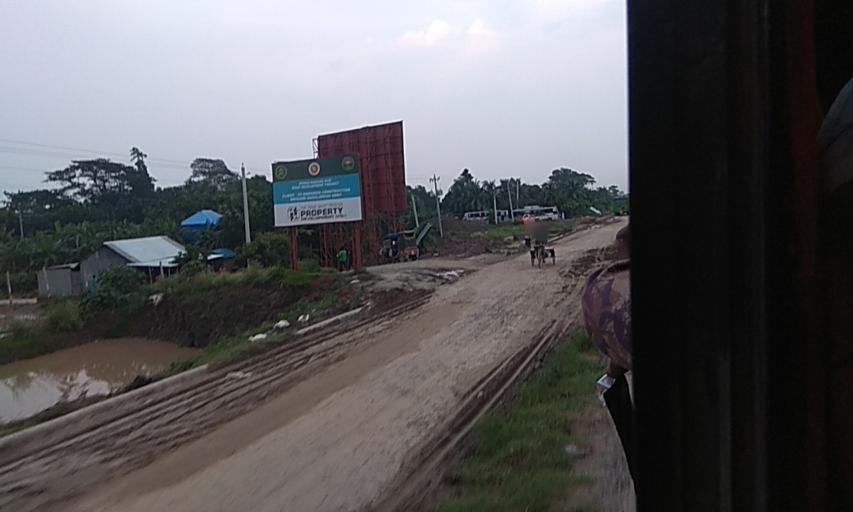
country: BD
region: Dhaka
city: Char Bhadrasan
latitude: 23.3794
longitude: 90.0088
